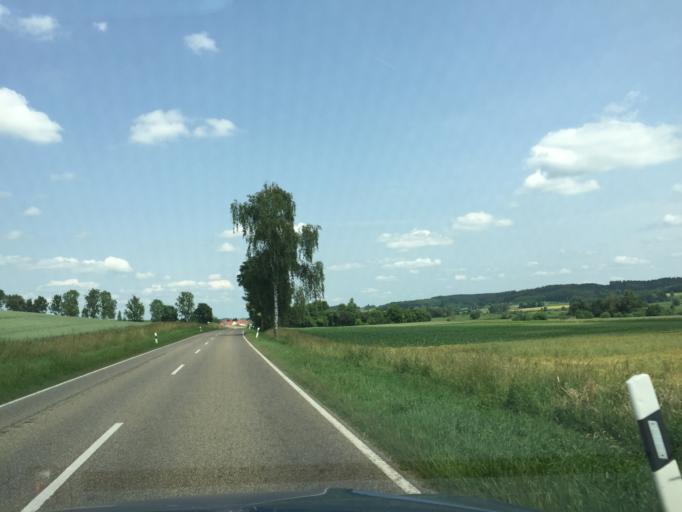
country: DE
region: Bavaria
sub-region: Swabia
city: Villenbach
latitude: 48.5168
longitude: 10.6222
